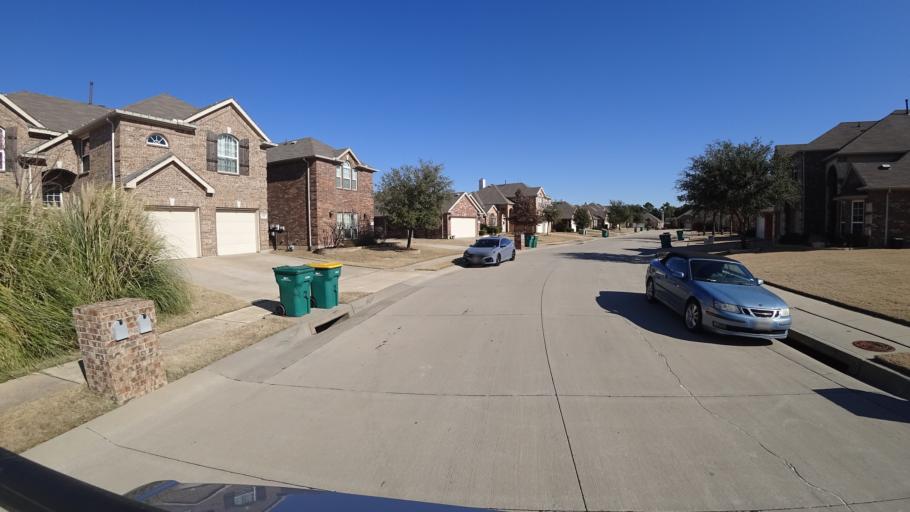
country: US
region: Texas
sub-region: Denton County
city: Lewisville
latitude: 33.0292
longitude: -97.0168
